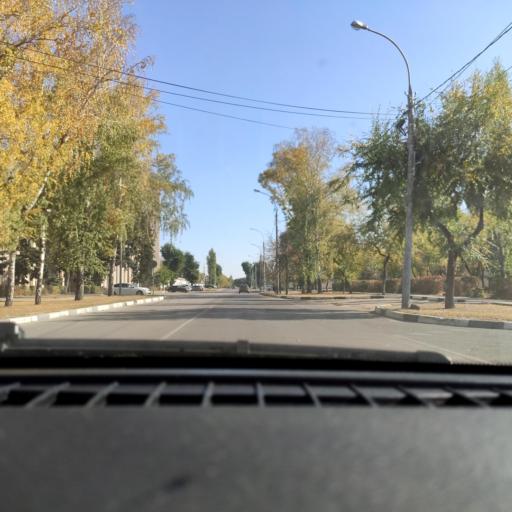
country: RU
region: Voronezj
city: Voronezh
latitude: 51.6368
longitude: 39.2489
